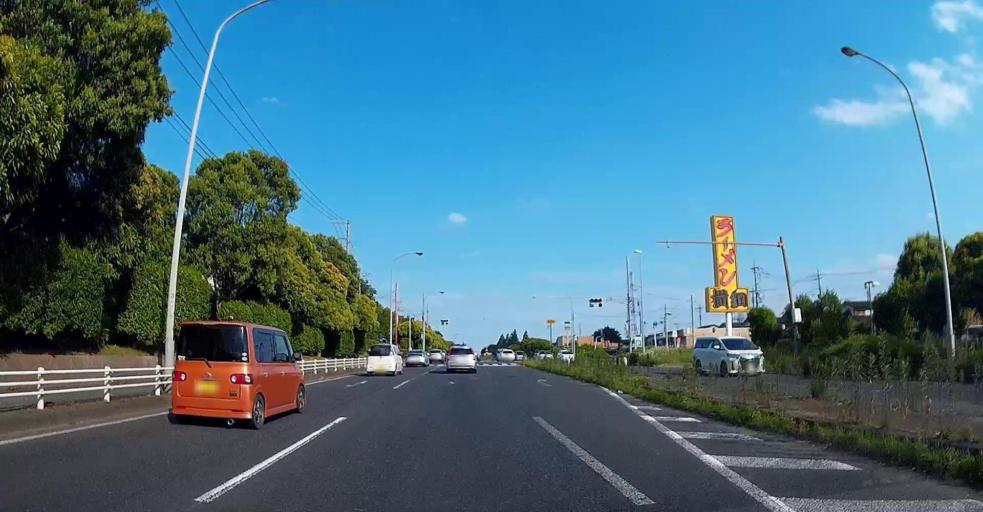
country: JP
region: Chiba
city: Shiroi
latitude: 35.7902
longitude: 140.0692
